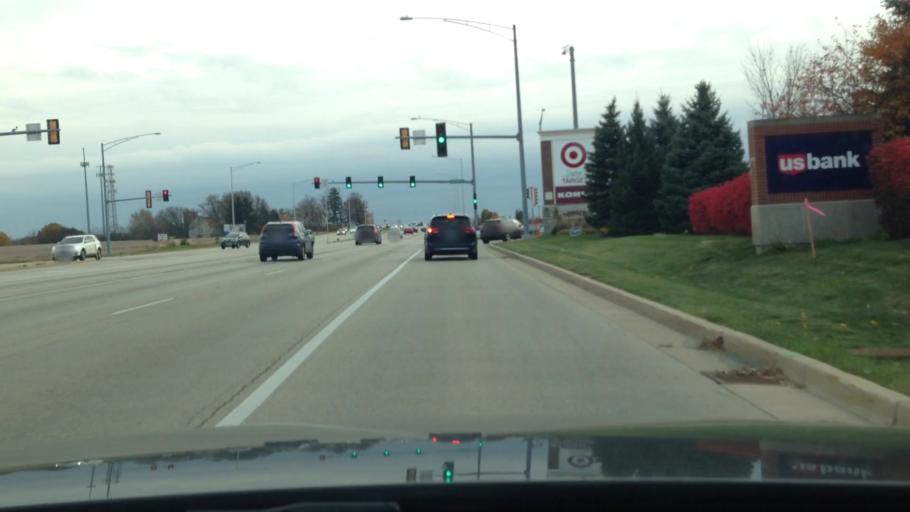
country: US
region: Illinois
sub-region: McHenry County
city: Lake in the Hills
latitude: 42.1620
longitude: -88.3358
